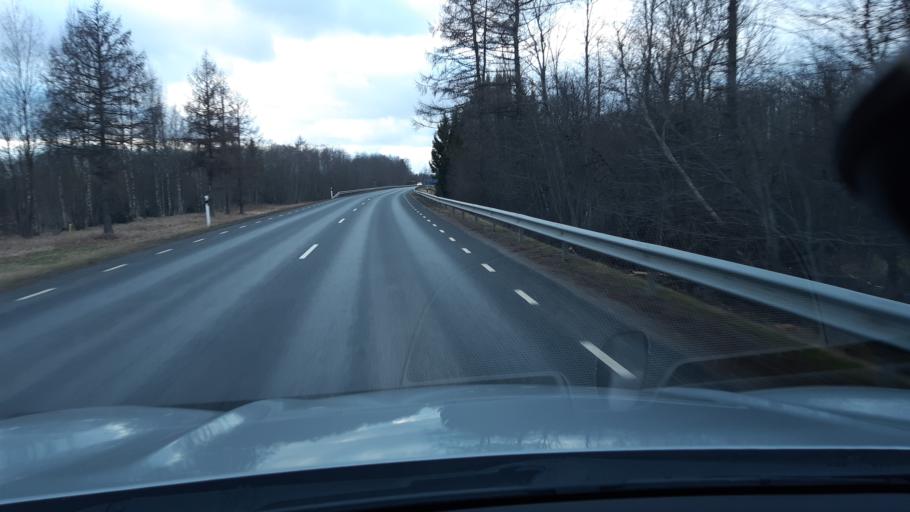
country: EE
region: Jaervamaa
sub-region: Tueri vald
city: Sarevere
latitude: 58.7997
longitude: 25.2519
